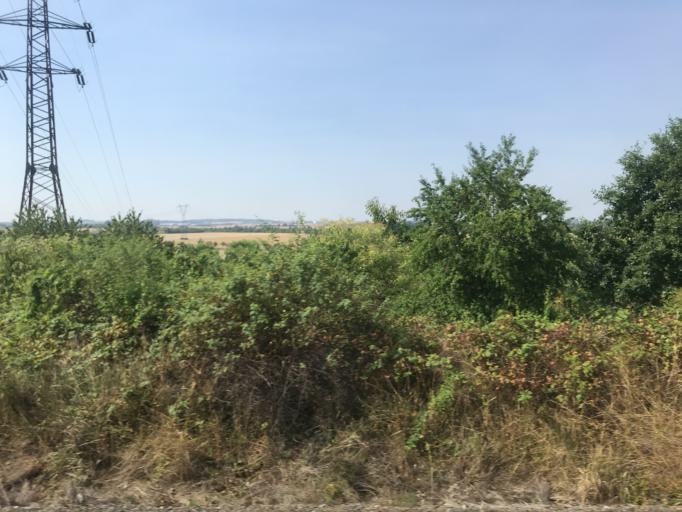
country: CZ
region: Central Bohemia
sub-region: Okres Praha-Vychod
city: Ricany
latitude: 50.0093
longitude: 14.6424
